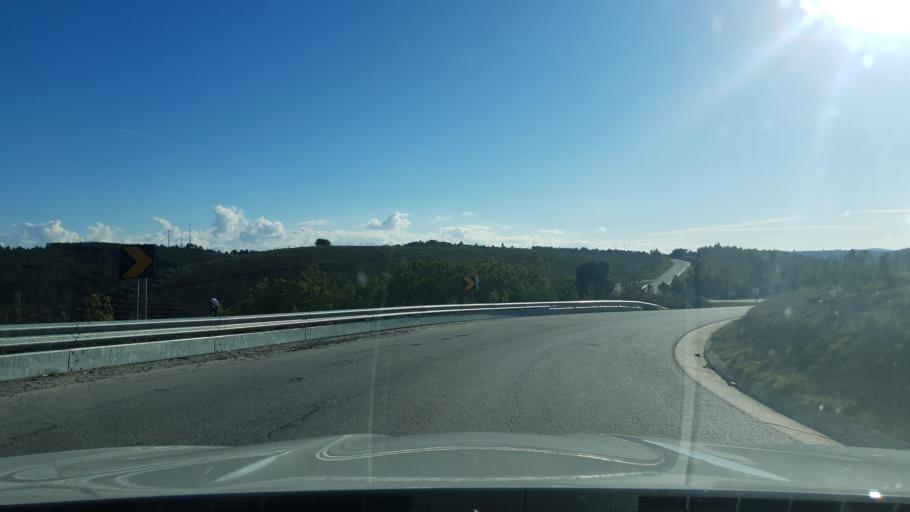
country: PT
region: Braganca
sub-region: Freixo de Espada A Cinta
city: Freixo de Espada a Cinta
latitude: 41.1265
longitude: -6.8153
